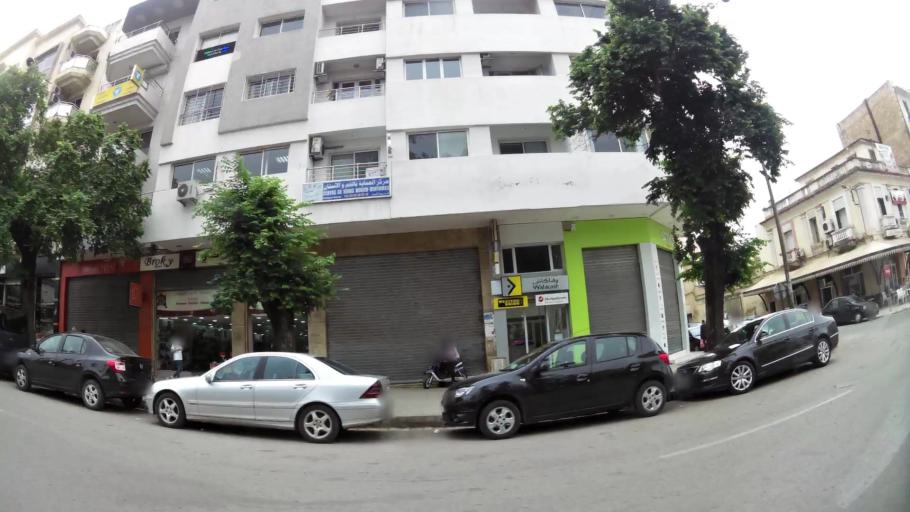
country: MA
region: Fes-Boulemane
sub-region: Fes
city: Fes
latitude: 34.0378
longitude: -4.9971
